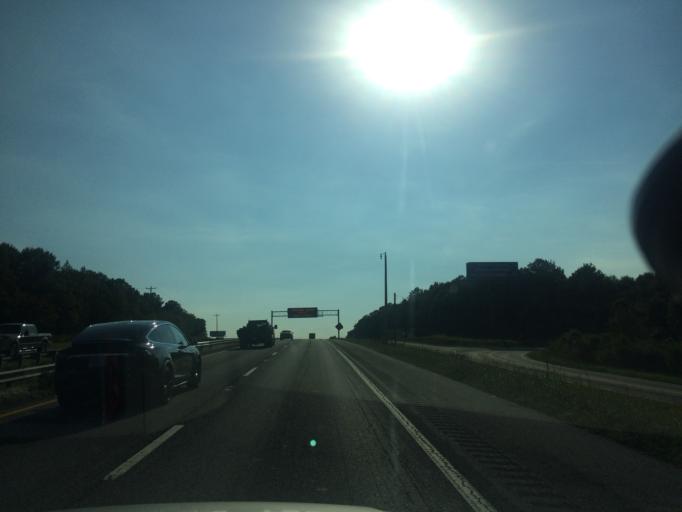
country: US
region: South Carolina
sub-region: Spartanburg County
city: Mayo
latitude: 35.0303
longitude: -81.8618
